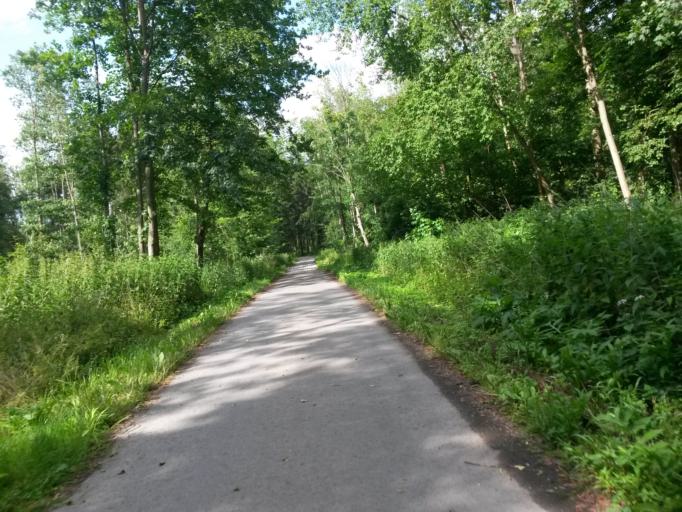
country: CZ
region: Olomoucky
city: Litovel
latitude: 49.6987
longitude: 17.1170
